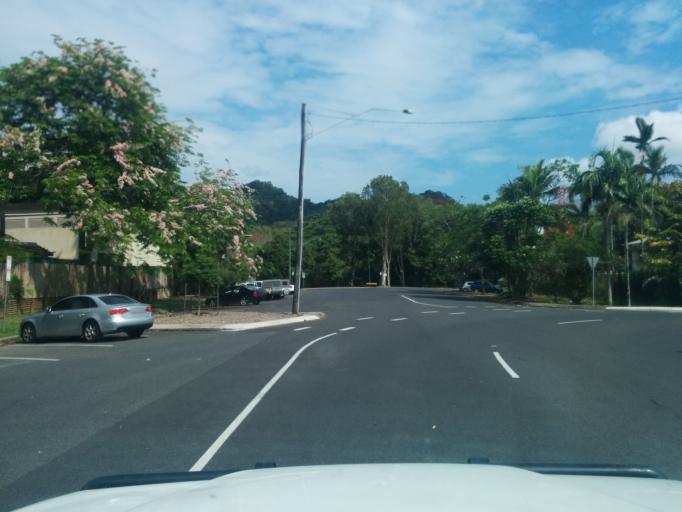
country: AU
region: Queensland
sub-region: Cairns
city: Cairns
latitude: -16.9019
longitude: 145.7549
